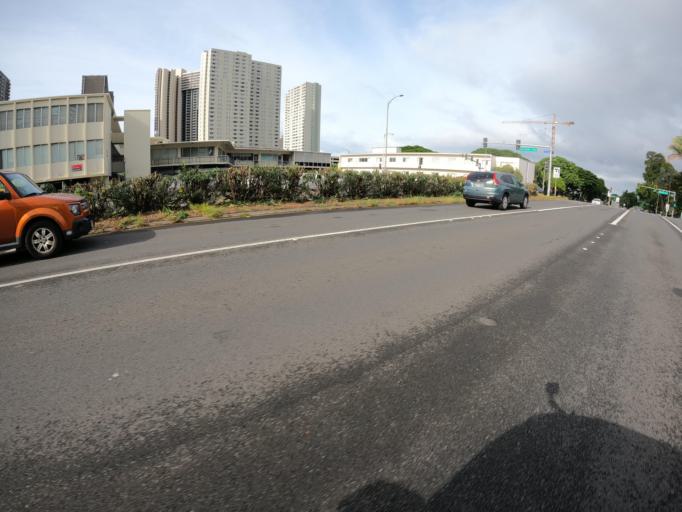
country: US
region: Hawaii
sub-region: Honolulu County
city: Honolulu
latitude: 21.3142
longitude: -157.8574
